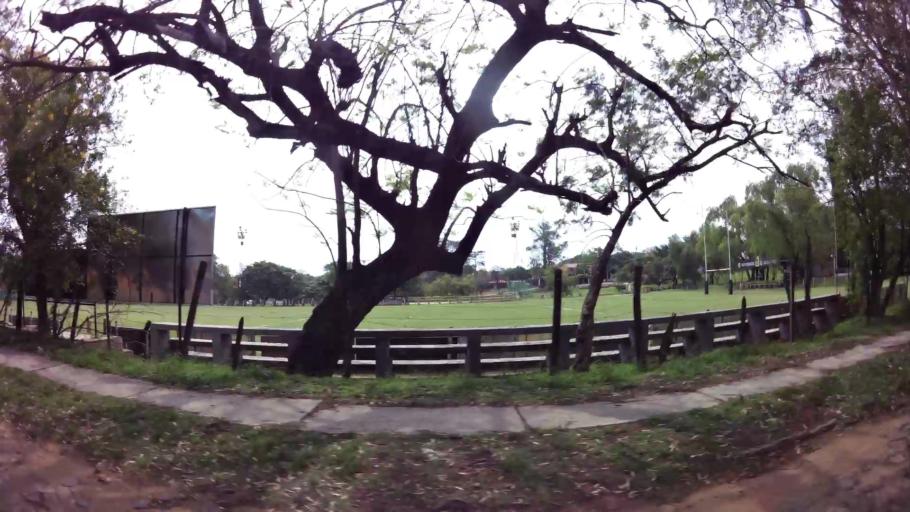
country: PY
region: Asuncion
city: Asuncion
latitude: -25.2725
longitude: -57.5684
